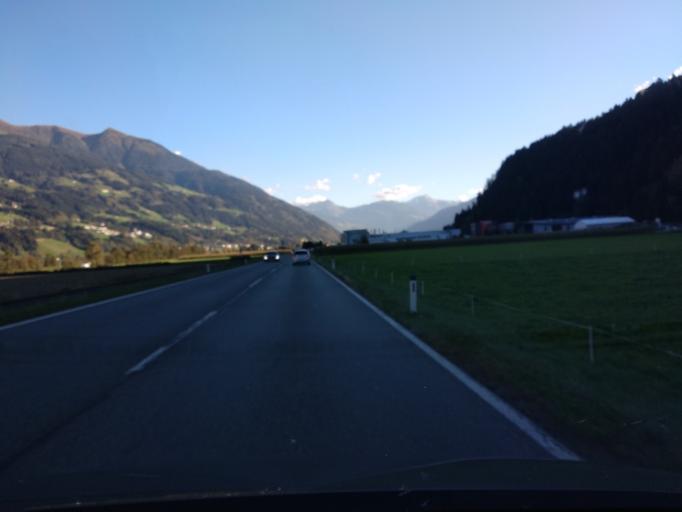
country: AT
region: Tyrol
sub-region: Politischer Bezirk Schwaz
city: Schlitters
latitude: 47.3707
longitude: 11.8475
